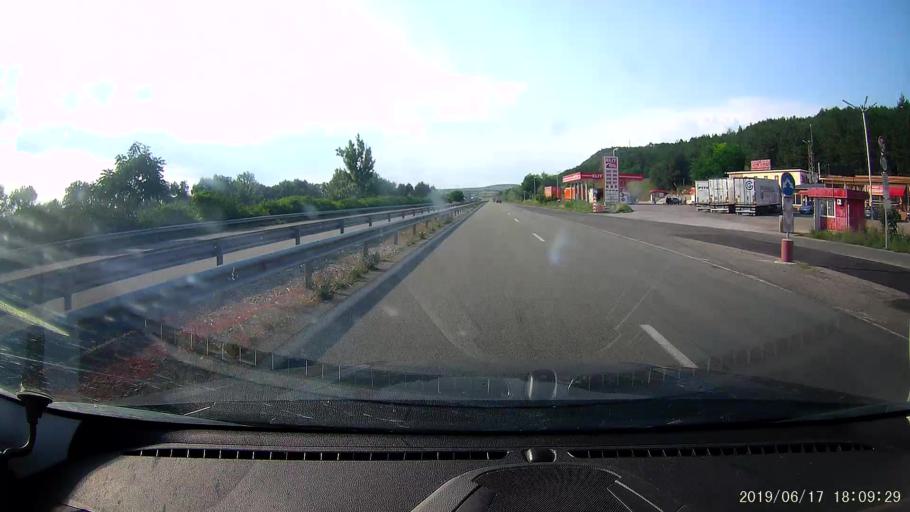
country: BG
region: Khaskovo
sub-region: Obshtina Lyubimets
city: Lyubimets
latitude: 41.8598
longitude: 26.0891
